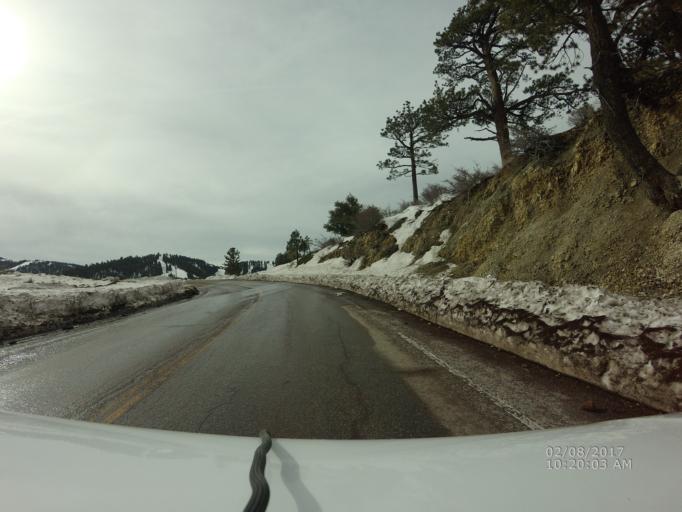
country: US
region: California
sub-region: San Bernardino County
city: Wrightwood
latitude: 34.3819
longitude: -117.6905
